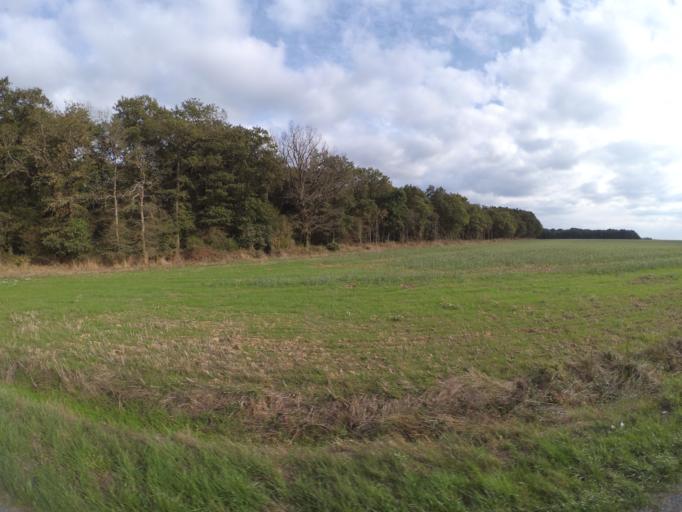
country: FR
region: Centre
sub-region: Departement d'Indre-et-Loire
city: Nazelles-Negron
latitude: 47.4659
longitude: 0.9388
